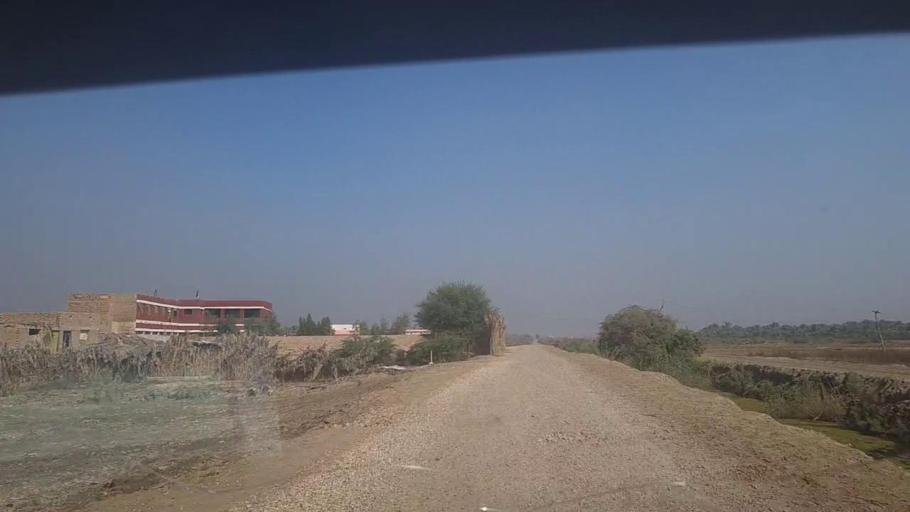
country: PK
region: Sindh
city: Khairpur
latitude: 27.4636
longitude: 68.7319
